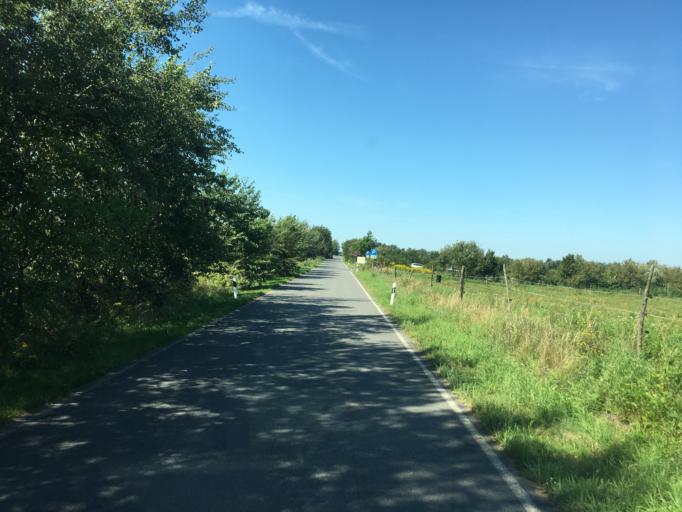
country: DE
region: Brandenburg
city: Welzow
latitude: 51.5260
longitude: 14.1739
